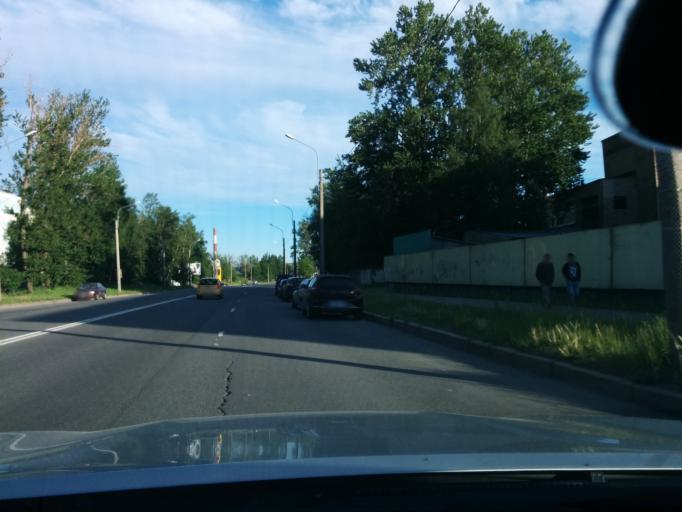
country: RU
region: St.-Petersburg
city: Kushelevka
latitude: 59.9814
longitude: 30.3649
